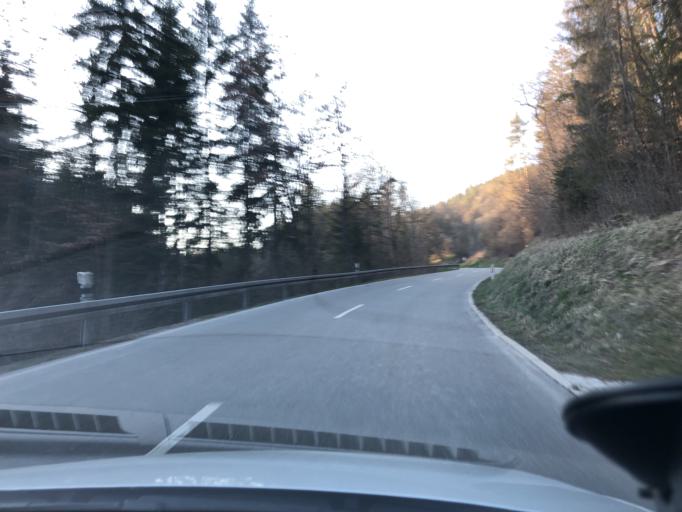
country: DE
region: Baden-Wuerttemberg
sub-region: Freiburg Region
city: Braunlingen
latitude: 47.8511
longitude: 8.4481
